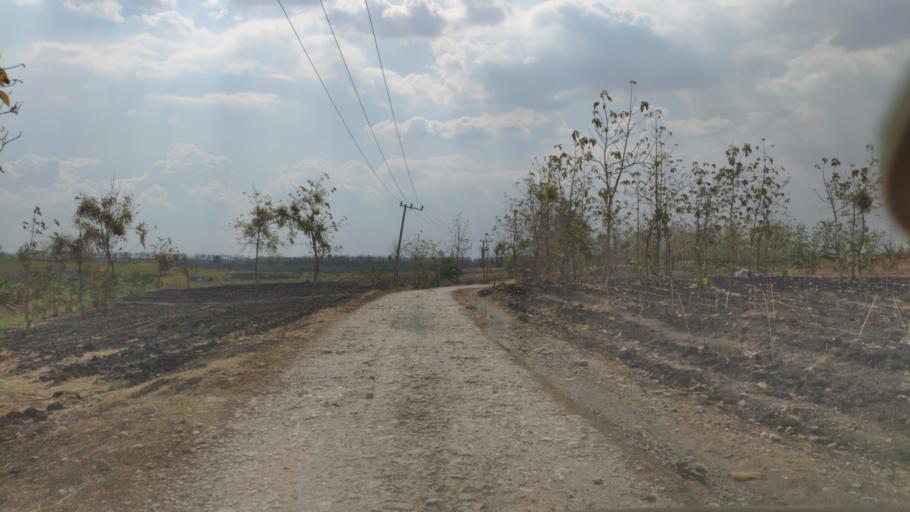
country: ID
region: Central Java
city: Mendenrejo
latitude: -7.3185
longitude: 111.3742
